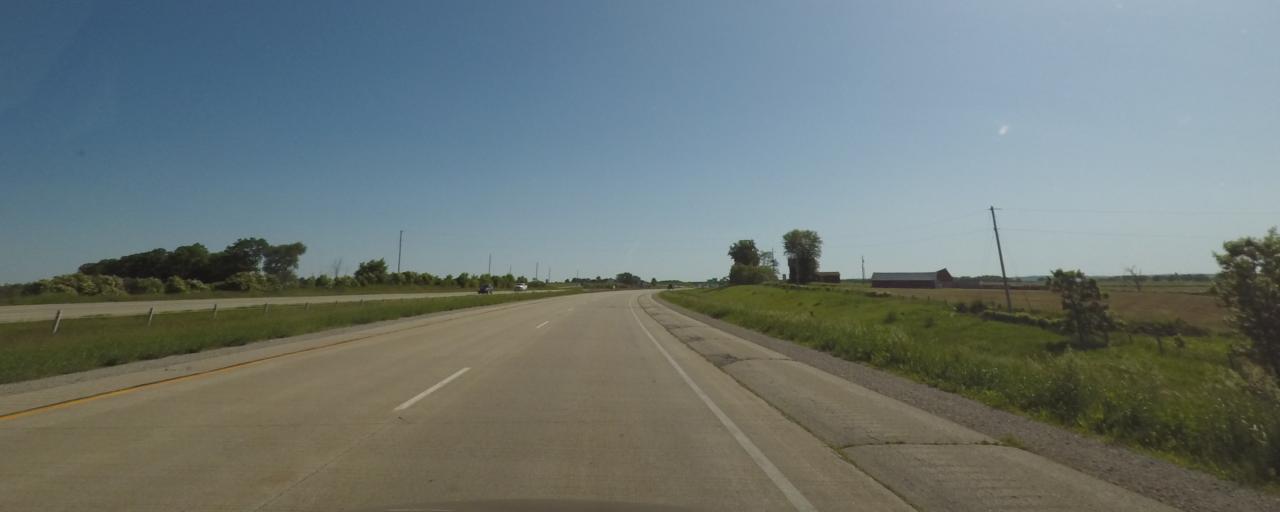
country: US
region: Wisconsin
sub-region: Fond du Lac County
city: Waupun
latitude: 43.5782
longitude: -88.7615
